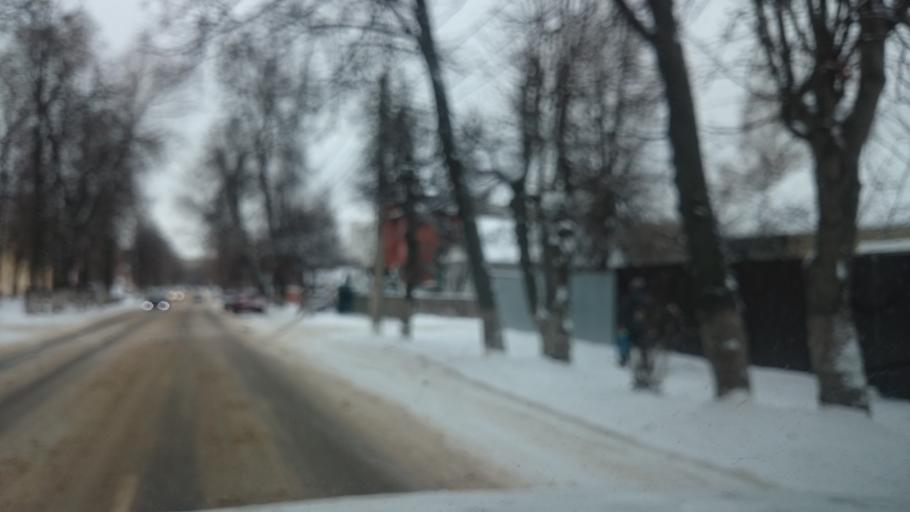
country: RU
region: Tula
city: Mendeleyevskiy
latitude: 54.1699
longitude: 37.5807
